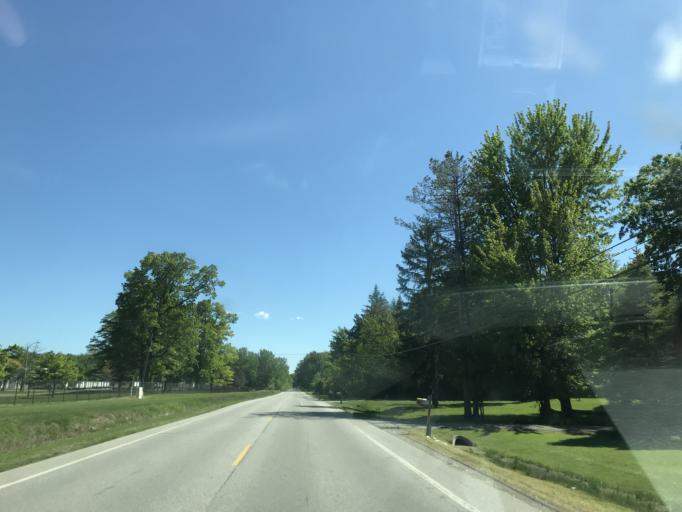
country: US
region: Michigan
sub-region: Wayne County
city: Woodhaven
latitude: 42.1769
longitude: -83.2866
